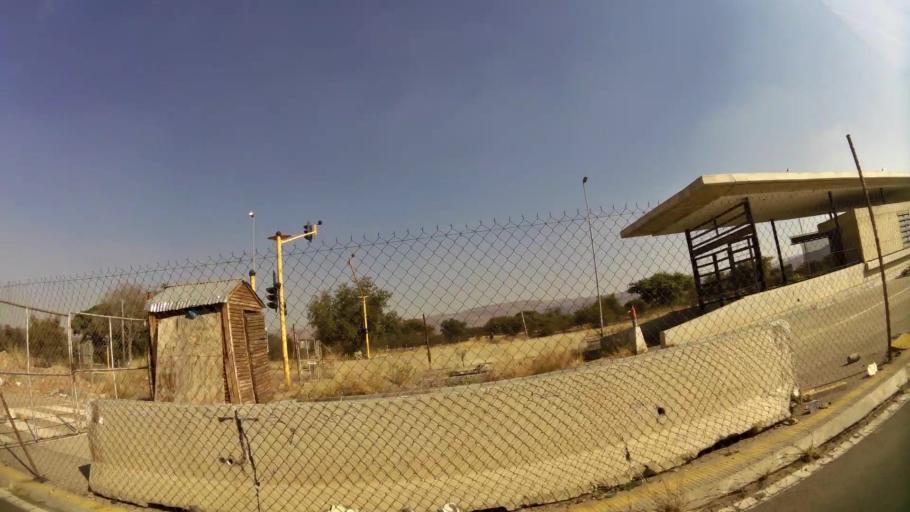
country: ZA
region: North-West
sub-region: Bojanala Platinum District Municipality
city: Rustenburg
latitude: -25.6611
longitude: 27.2303
